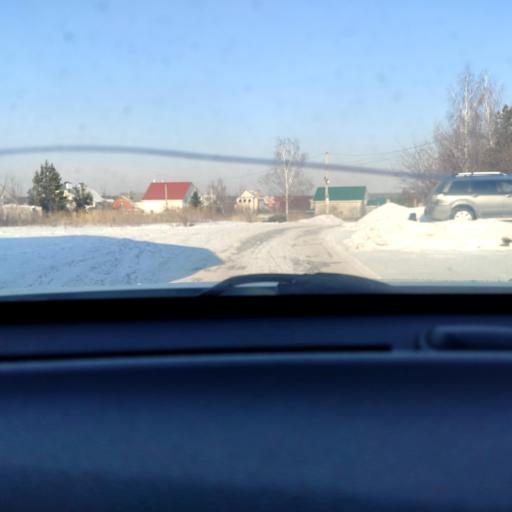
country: RU
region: Voronezj
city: Somovo
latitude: 51.6816
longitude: 39.3162
